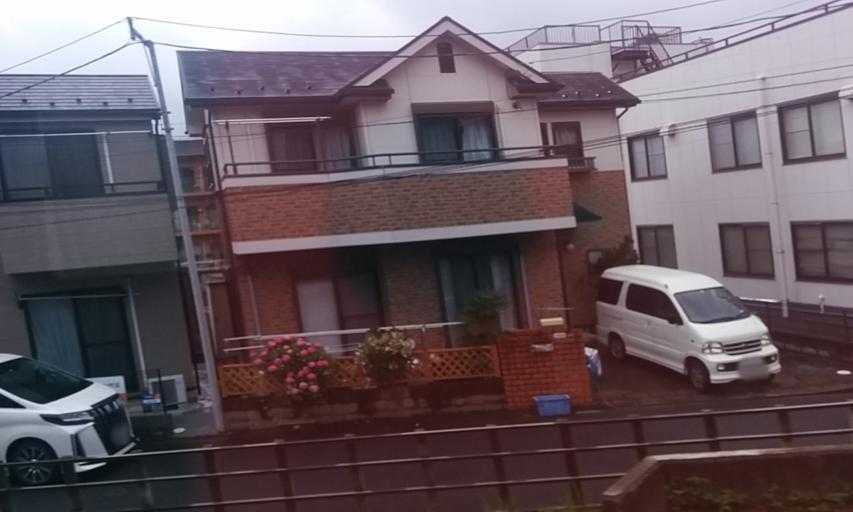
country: JP
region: Tokyo
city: Hino
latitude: 35.6590
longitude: 139.4251
